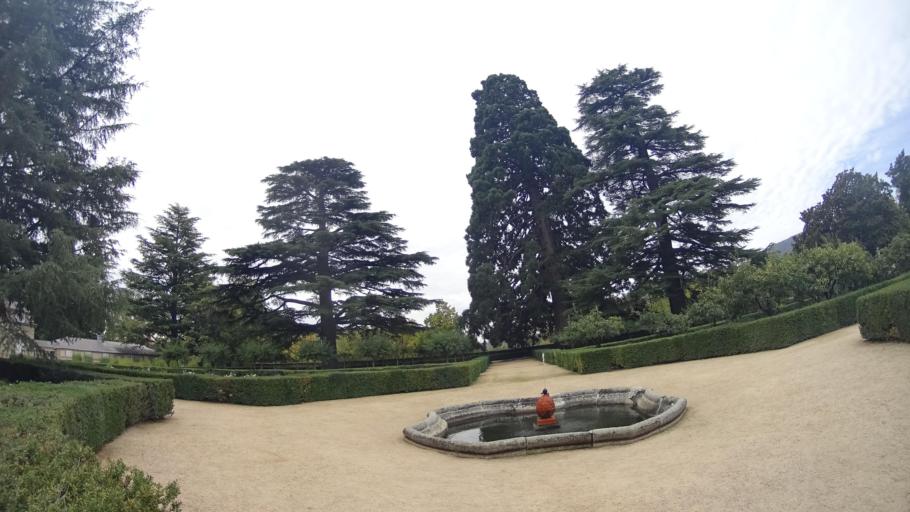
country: ES
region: Madrid
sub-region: Provincia de Madrid
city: El Escorial
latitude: 40.5846
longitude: -4.1372
